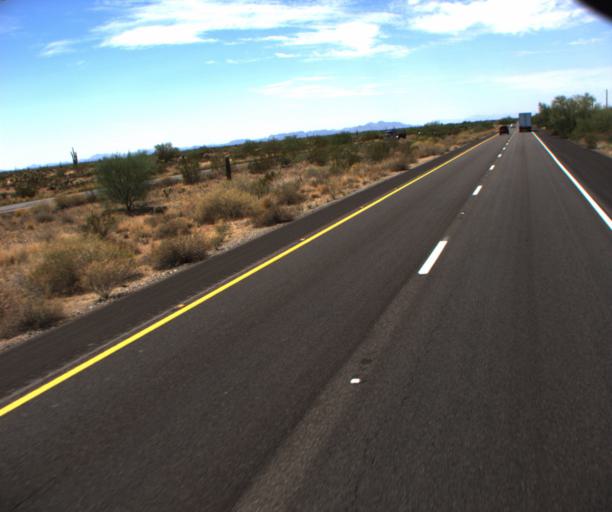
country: US
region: Arizona
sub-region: Pinal County
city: Gold Camp
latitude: 33.2578
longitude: -111.3124
